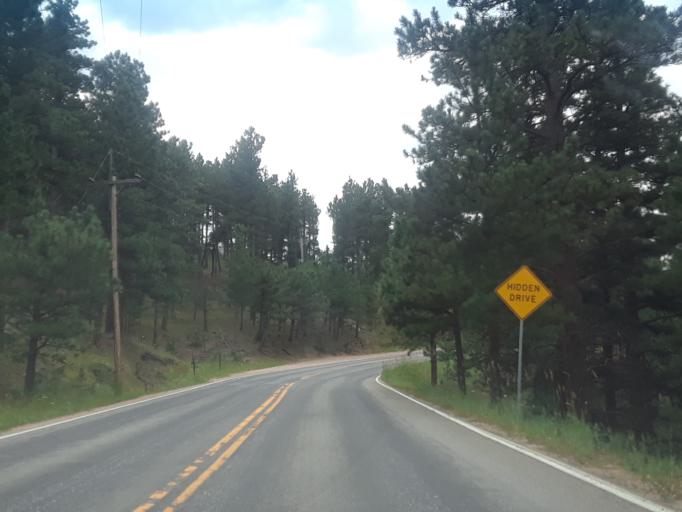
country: US
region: Colorado
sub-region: Boulder County
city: Boulder
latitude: 40.0437
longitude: -105.3296
